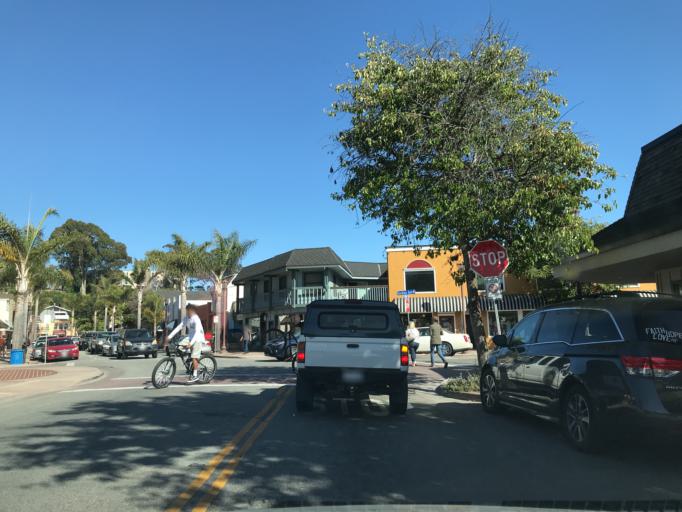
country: US
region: California
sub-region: Santa Cruz County
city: Capitola
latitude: 36.9733
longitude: -121.9523
